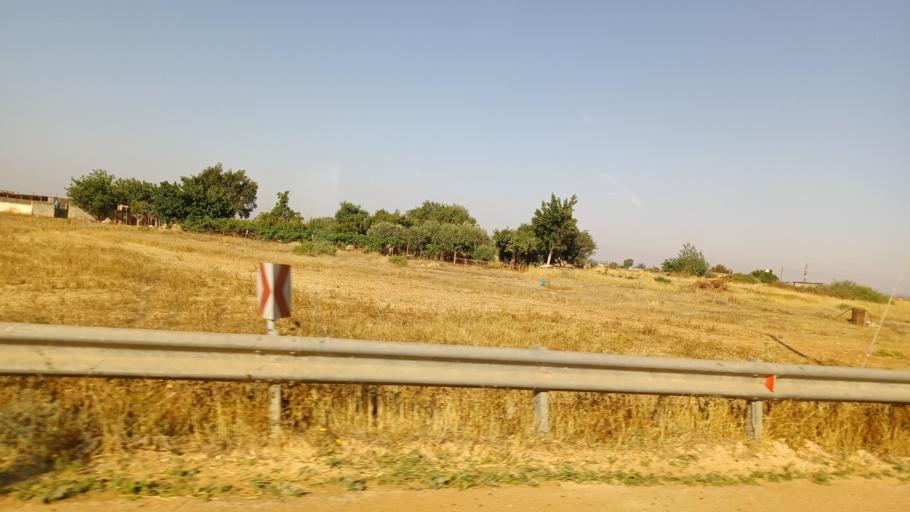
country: CY
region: Ammochostos
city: Frenaros
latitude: 35.0553
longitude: 33.9112
